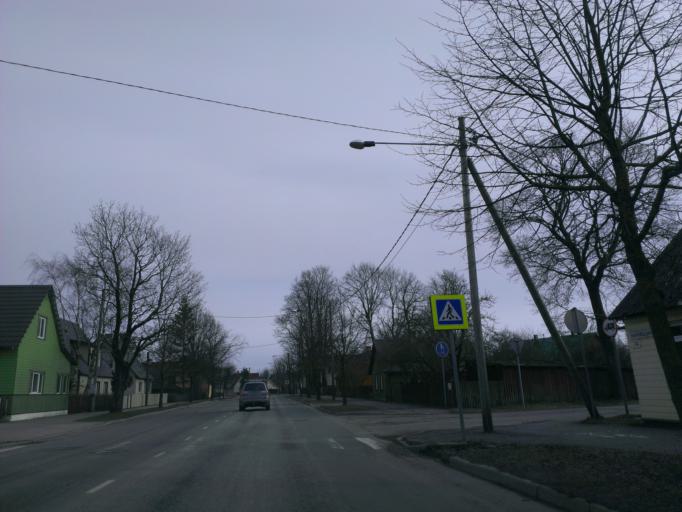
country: EE
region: Paernumaa
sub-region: Paernu linn
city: Parnu
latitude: 58.3913
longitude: 24.4656
